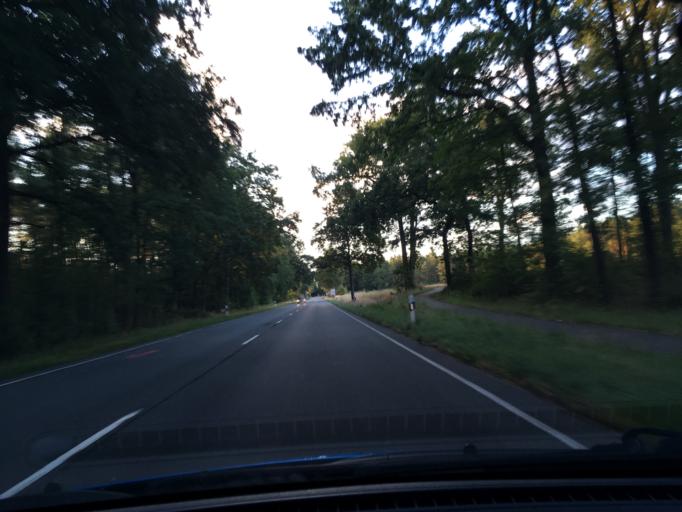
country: DE
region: Lower Saxony
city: Bergen
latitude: 52.7425
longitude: 9.9775
